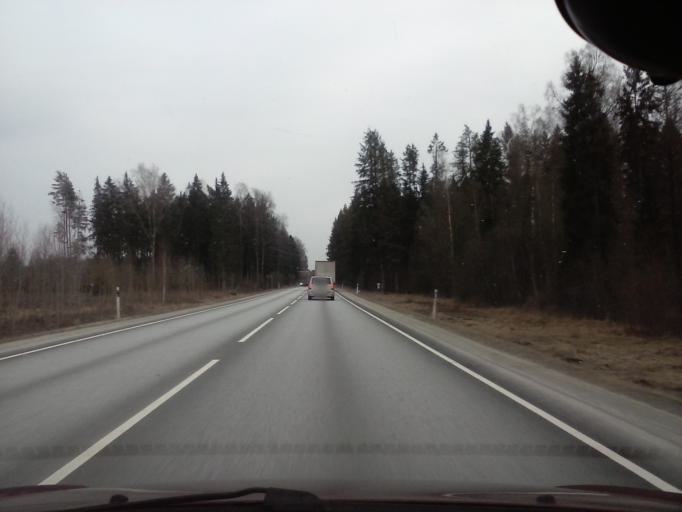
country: EE
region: Jaervamaa
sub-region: Paide linn
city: Paide
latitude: 58.9815
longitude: 25.5937
